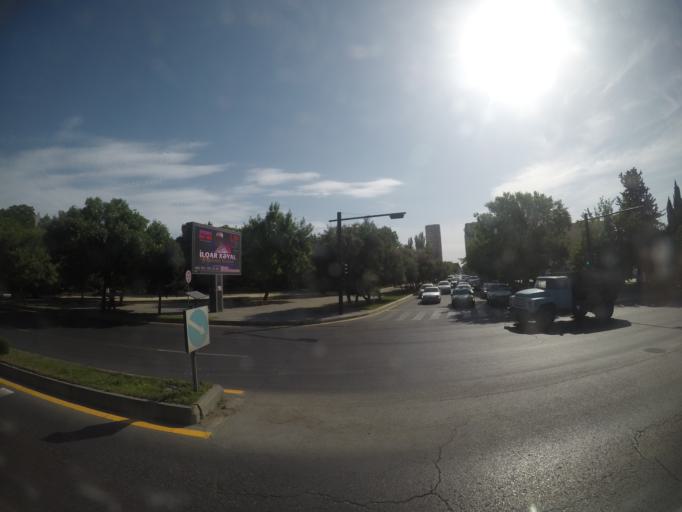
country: AZ
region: Baki
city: Badamdar
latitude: 40.3893
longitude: 49.8256
